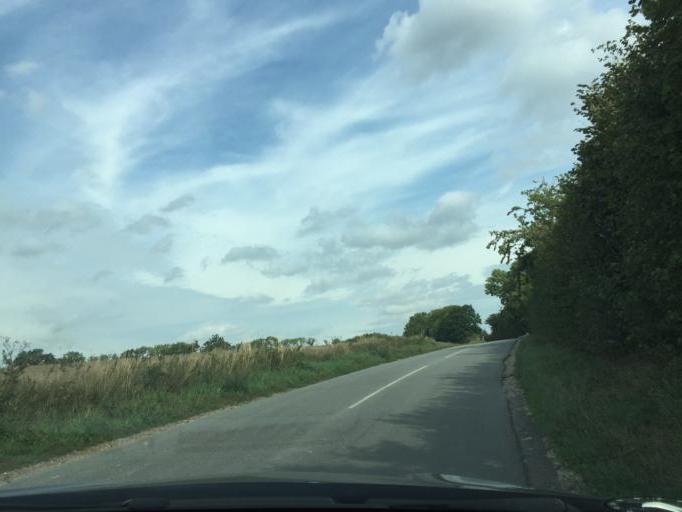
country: DK
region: South Denmark
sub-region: Assens Kommune
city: Vissenbjerg
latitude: 55.3834
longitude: 10.1752
